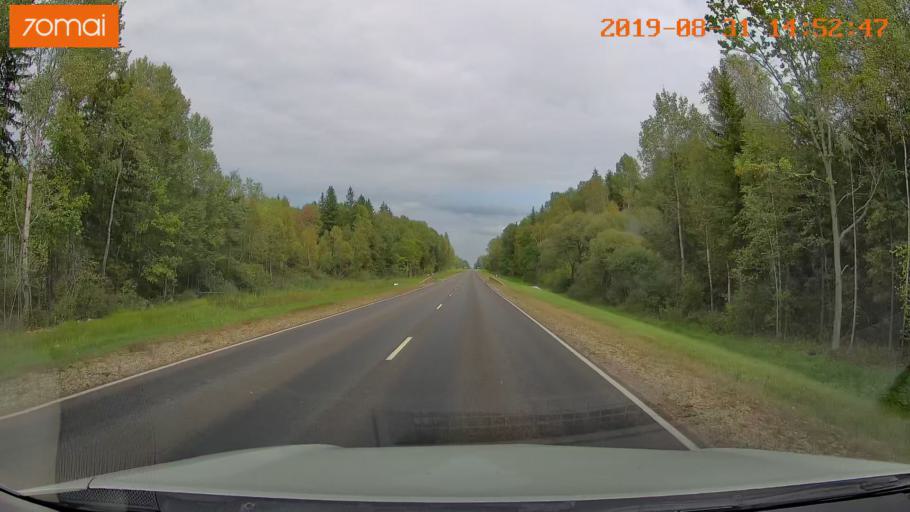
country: RU
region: Kaluga
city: Spas-Demensk
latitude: 54.2785
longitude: 33.8481
